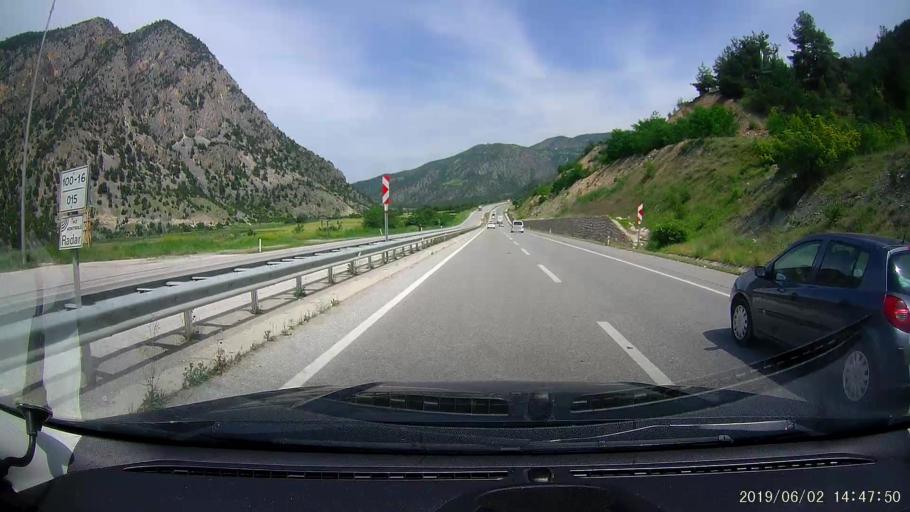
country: TR
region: Corum
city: Hacihamza
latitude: 41.0658
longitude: 34.4685
